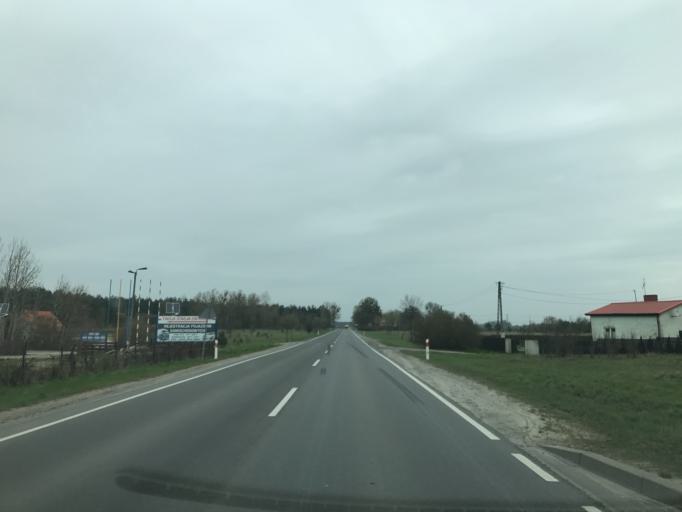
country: PL
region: Warmian-Masurian Voivodeship
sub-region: Powiat olsztynski
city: Olsztynek
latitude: 53.5934
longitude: 20.2973
